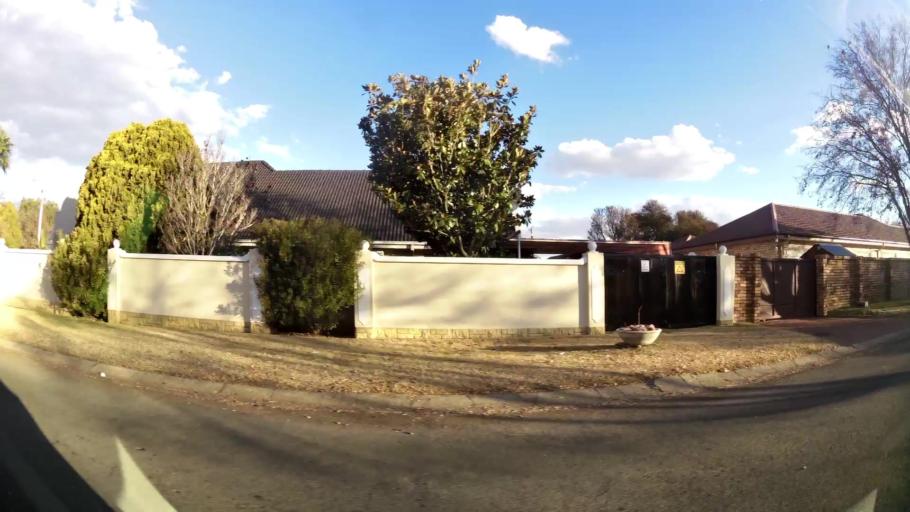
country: ZA
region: North-West
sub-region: Dr Kenneth Kaunda District Municipality
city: Potchefstroom
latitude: -26.7318
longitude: 27.0962
